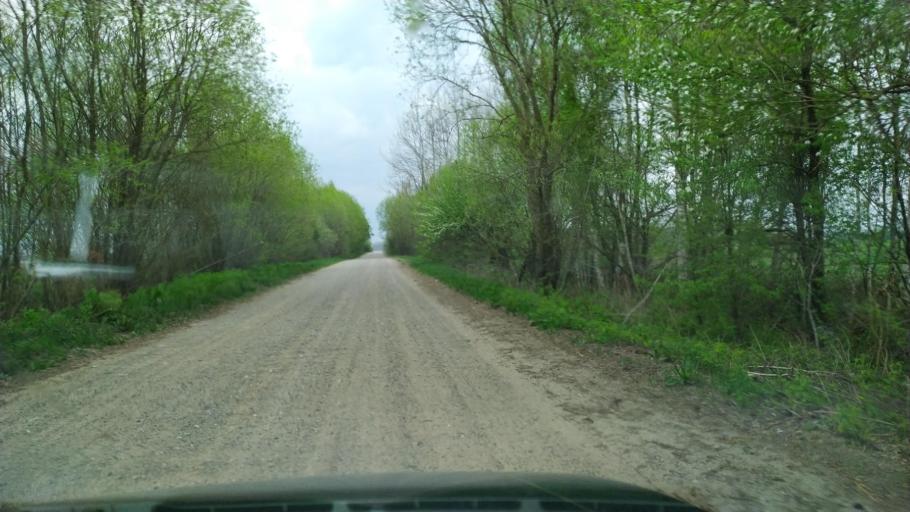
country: BY
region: Brest
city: Zhabinka
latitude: 52.1387
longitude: 24.0909
